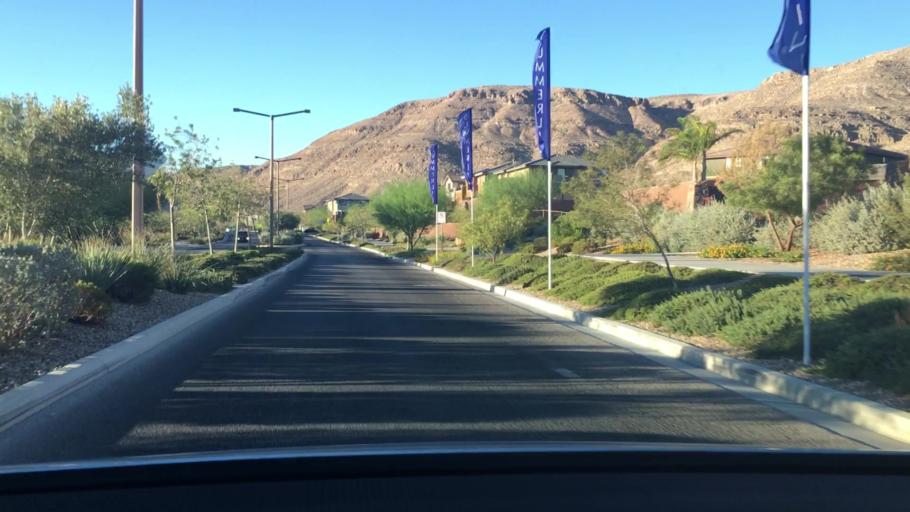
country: US
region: Nevada
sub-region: Clark County
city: Summerlin South
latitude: 36.0827
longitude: -115.3206
